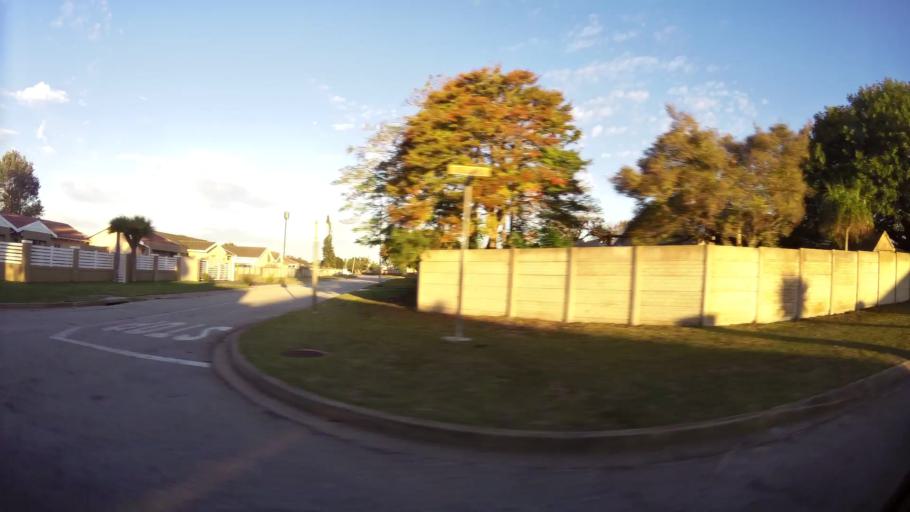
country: ZA
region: Eastern Cape
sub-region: Nelson Mandela Bay Metropolitan Municipality
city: Port Elizabeth
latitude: -33.9723
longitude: 25.5195
